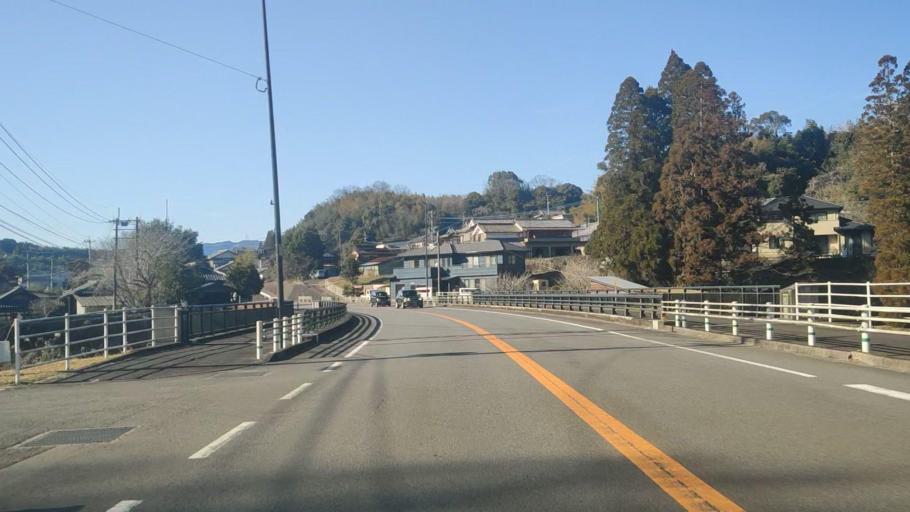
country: JP
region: Oita
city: Usuki
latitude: 33.0645
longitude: 131.6619
